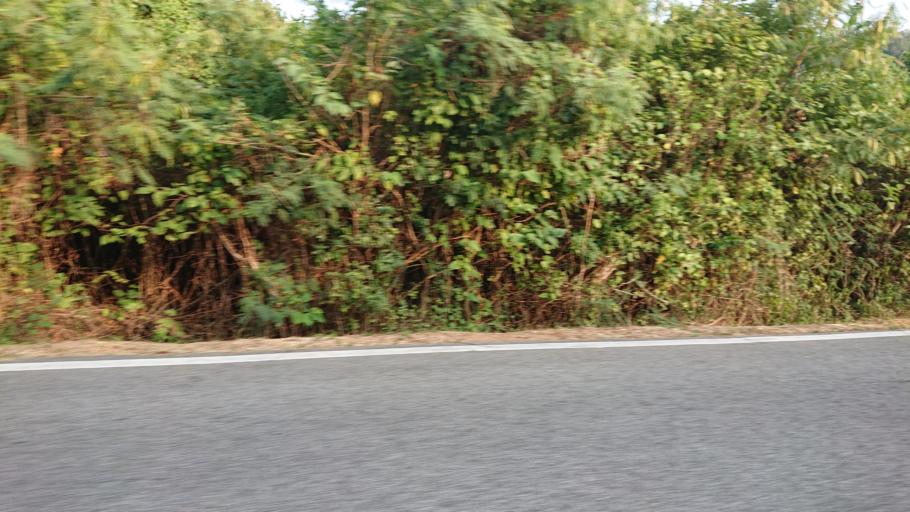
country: TW
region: Fukien
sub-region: Kinmen
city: Jincheng
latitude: 24.4350
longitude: 118.2489
